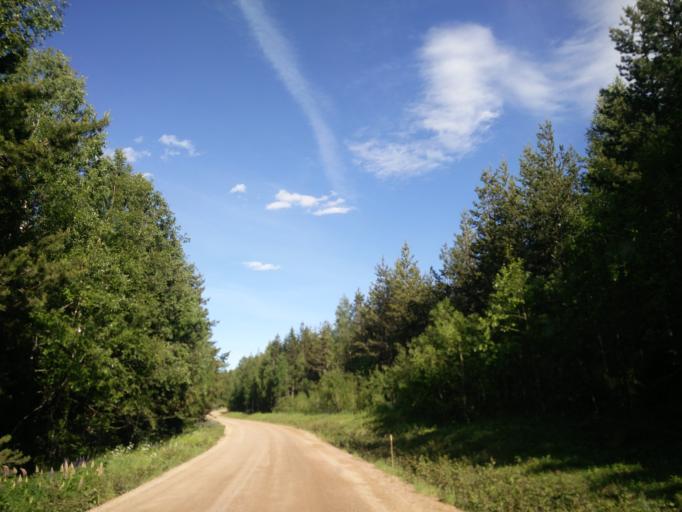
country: SE
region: Gaevleborg
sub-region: Hudiksvalls Kommun
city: Delsbo
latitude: 62.1867
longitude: 16.4590
